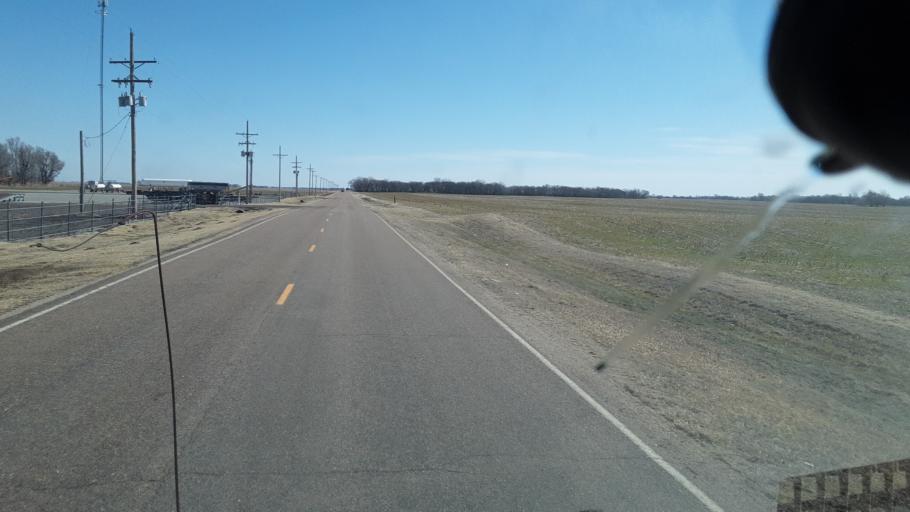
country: US
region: Kansas
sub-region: Rice County
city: Sterling
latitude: 38.2462
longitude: -98.3049
